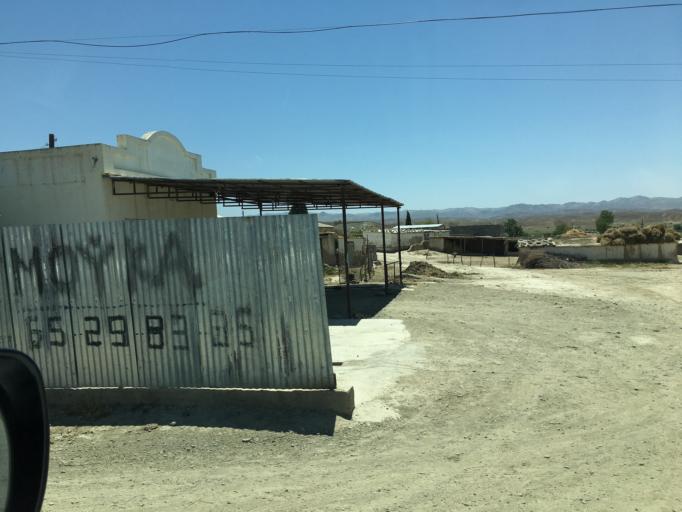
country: TM
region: Balkan
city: Magtymguly
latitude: 38.4288
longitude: 56.3262
